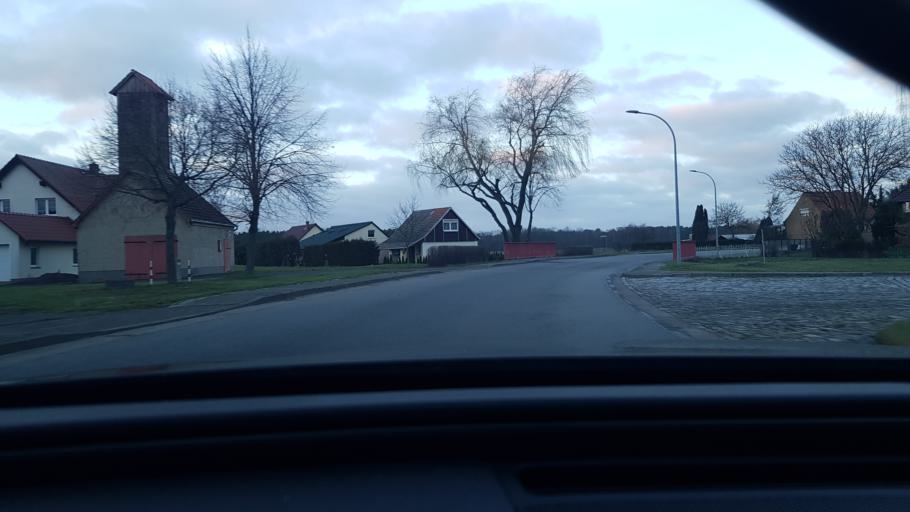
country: DE
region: Brandenburg
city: Storkow
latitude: 52.2810
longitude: 13.9039
